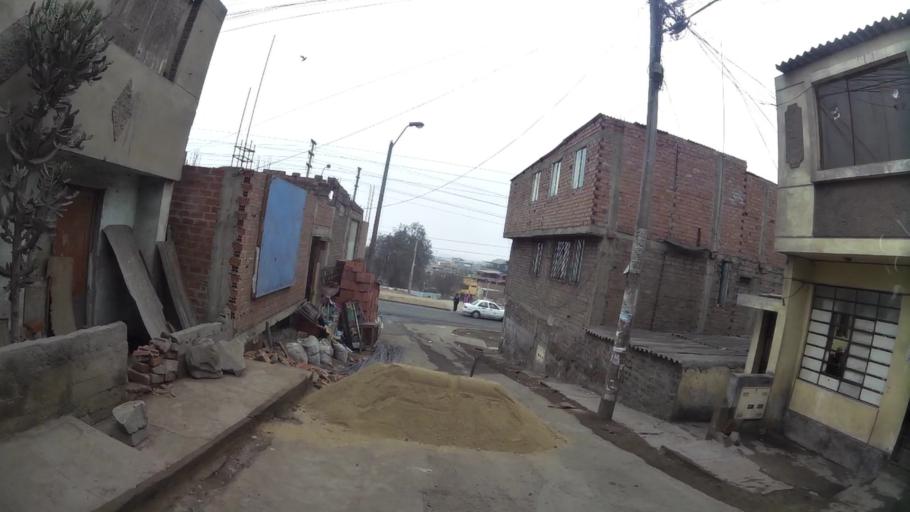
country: PE
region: Lima
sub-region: Lima
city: Surco
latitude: -12.1537
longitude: -76.9627
